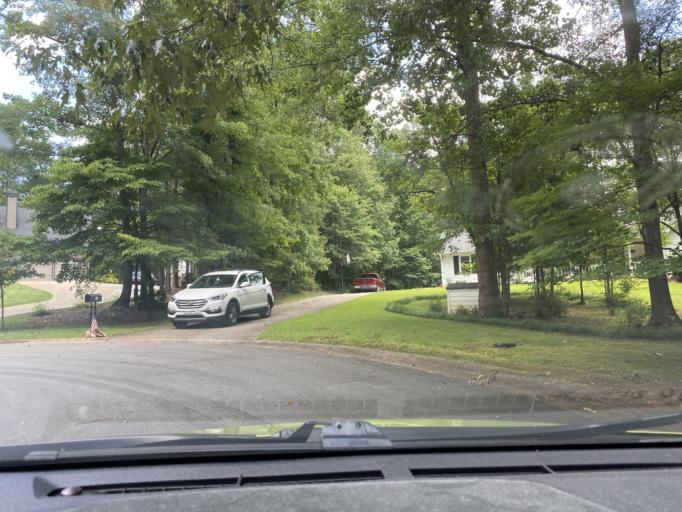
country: US
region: Georgia
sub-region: Fulton County
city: Palmetto
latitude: 33.4387
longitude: -84.6793
